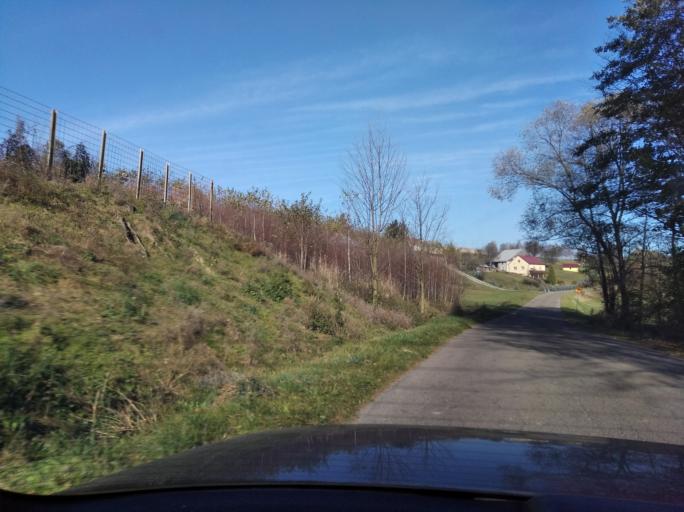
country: PL
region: Subcarpathian Voivodeship
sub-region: Powiat ropczycko-sedziszowski
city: Wielopole Skrzynskie
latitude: 49.9089
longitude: 21.5663
